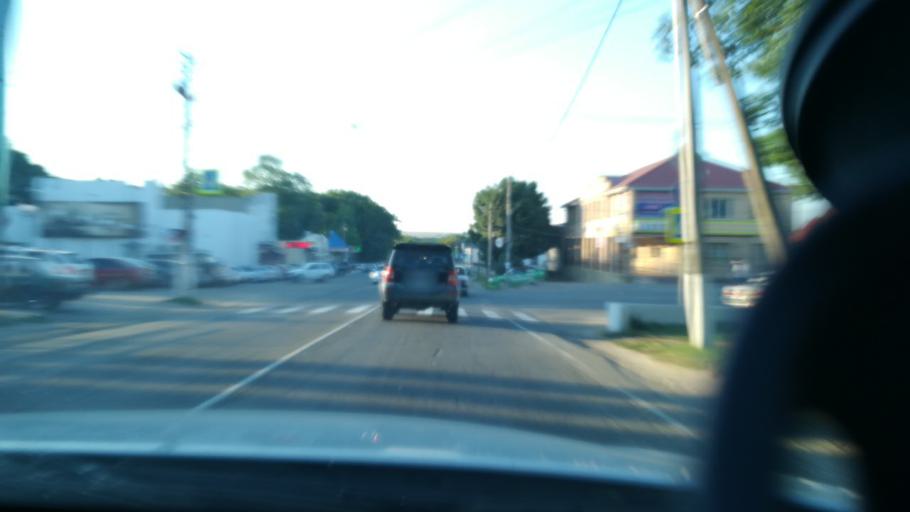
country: RU
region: Krasnodarskiy
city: Gostagayevskaya
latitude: 45.0235
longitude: 37.5030
